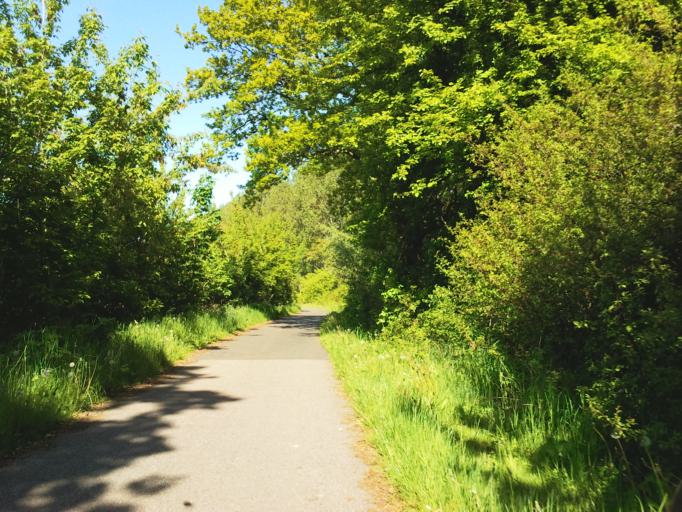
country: DE
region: Mecklenburg-Vorpommern
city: Nienhagen
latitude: 54.1295
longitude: 12.1751
